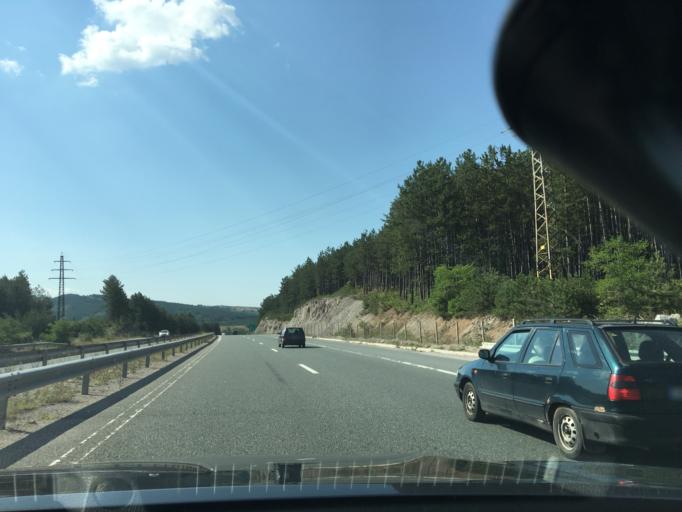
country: BG
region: Pernik
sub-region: Obshtina Pernik
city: Pernik
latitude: 42.5104
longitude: 23.1412
